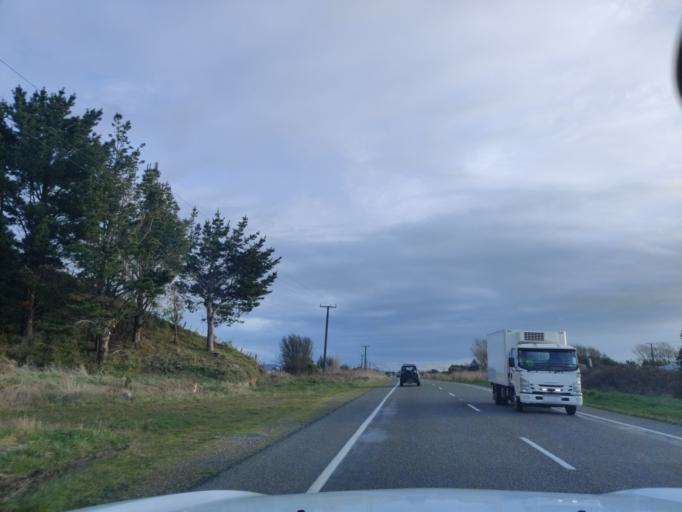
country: NZ
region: Manawatu-Wanganui
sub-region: Horowhenua District
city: Foxton
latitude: -40.5365
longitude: 175.4258
